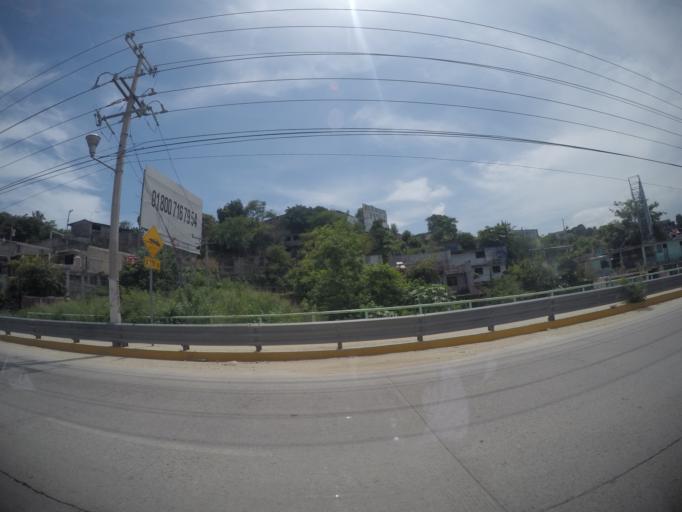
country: MX
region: Guerrero
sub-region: Acapulco de Juarez
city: Colonia Nueva Revolucion
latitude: 16.9116
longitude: -99.8248
